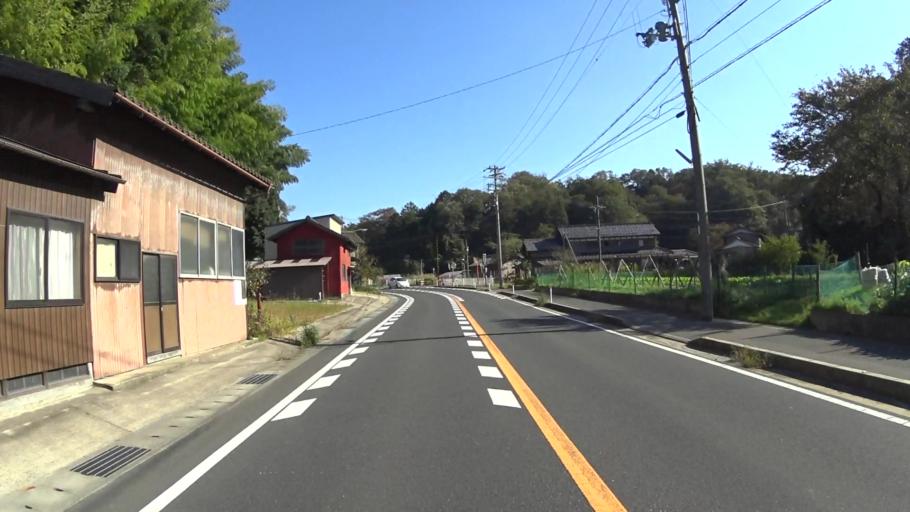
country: JP
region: Kyoto
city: Miyazu
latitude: 35.6471
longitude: 135.0442
